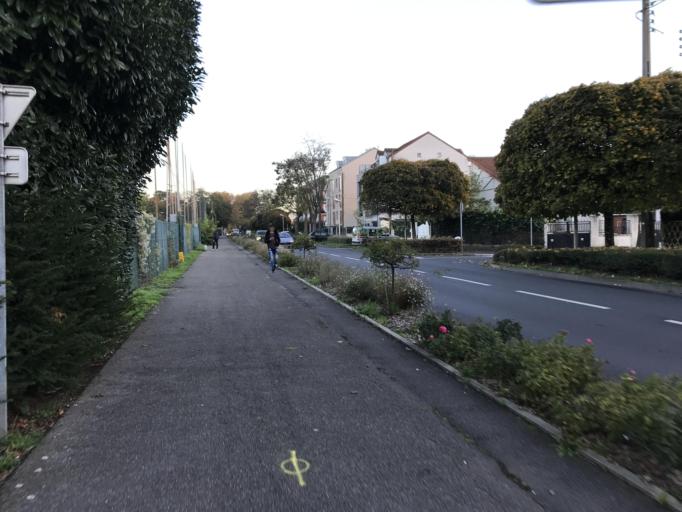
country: FR
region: Ile-de-France
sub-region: Departement de l'Essonne
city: Athis-Mons
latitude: 48.7120
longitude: 2.3806
